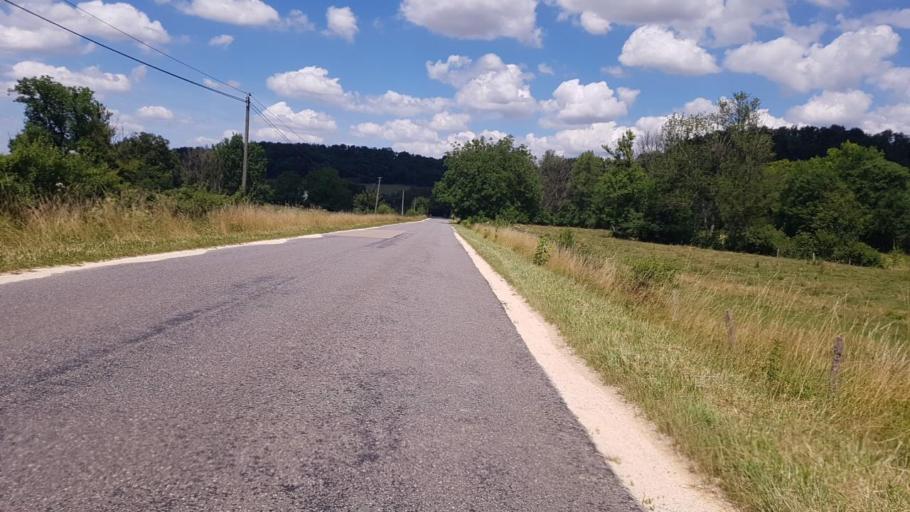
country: FR
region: Lorraine
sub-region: Departement de la Meuse
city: Ligny-en-Barrois
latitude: 48.6380
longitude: 5.4490
